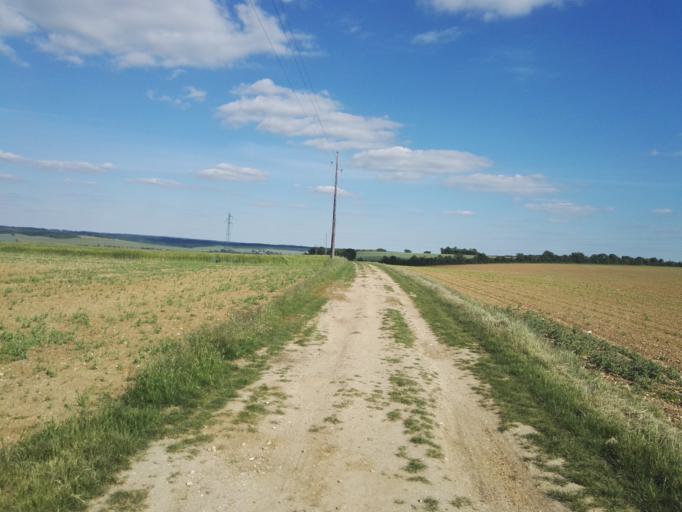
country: FR
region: Haute-Normandie
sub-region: Departement de l'Eure
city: Pacy-sur-Eure
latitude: 48.9893
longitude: 1.3729
